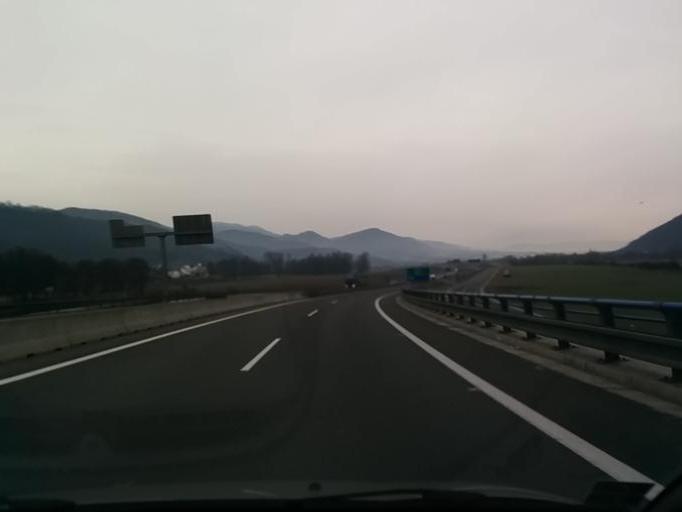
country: SK
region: Banskobystricky
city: Zarnovica
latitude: 48.5035
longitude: 18.7316
